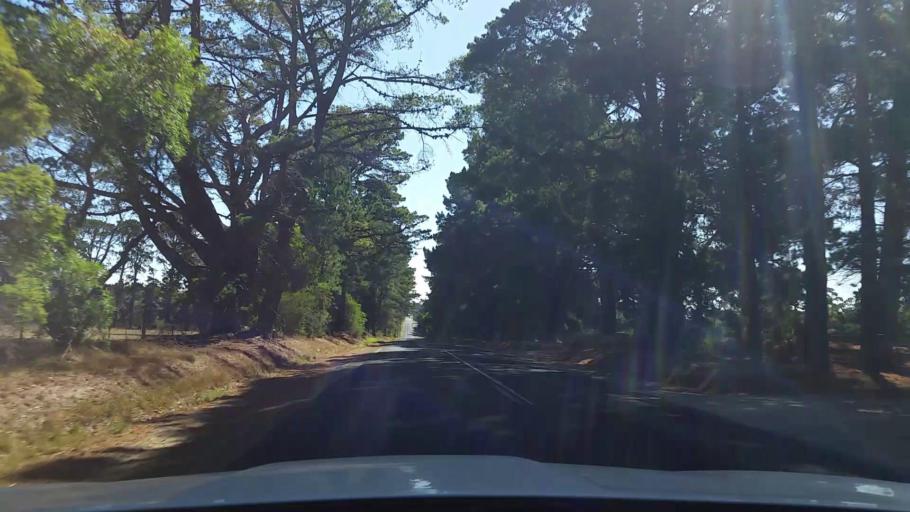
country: AU
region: Victoria
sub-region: Mornington Peninsula
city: Balnarring
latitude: -38.3517
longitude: 145.1457
